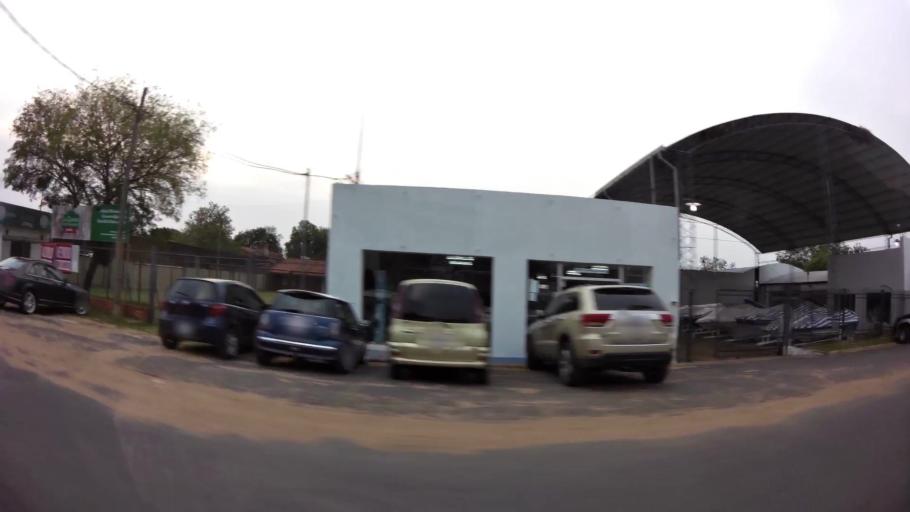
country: PY
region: Central
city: Lambare
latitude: -25.3565
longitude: -57.6439
